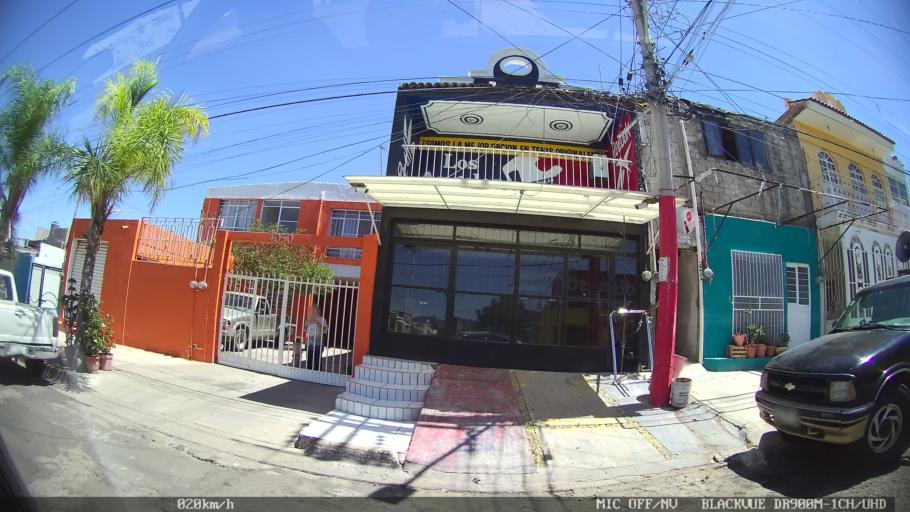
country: MX
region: Jalisco
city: Tlaquepaque
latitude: 20.6776
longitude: -103.2716
